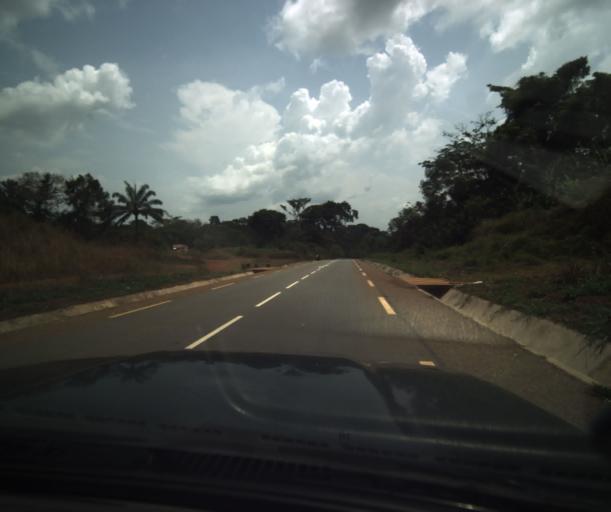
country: CM
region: Centre
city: Mbankomo
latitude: 3.6786
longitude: 11.3508
